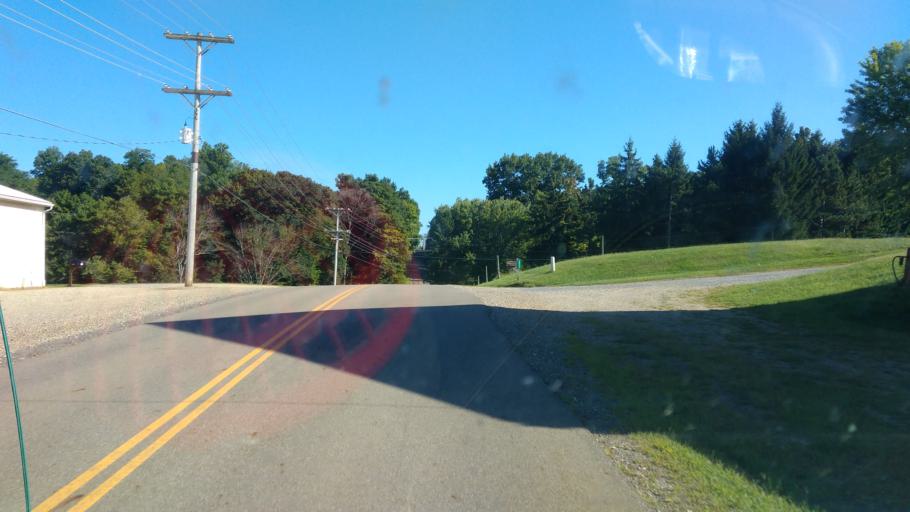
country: US
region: Ohio
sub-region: Knox County
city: Gambier
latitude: 40.4605
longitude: -82.3653
